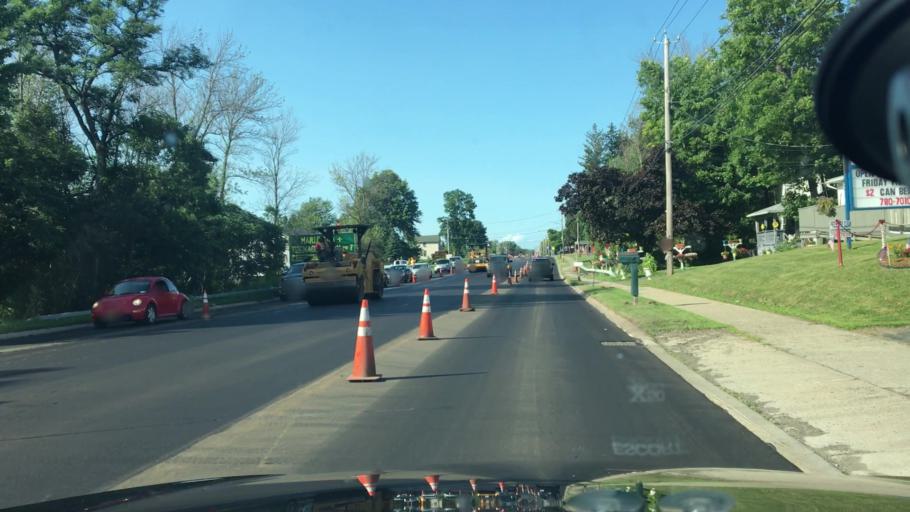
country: US
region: New York
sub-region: Erie County
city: Angola on the Lake
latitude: 42.6403
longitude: -79.0468
